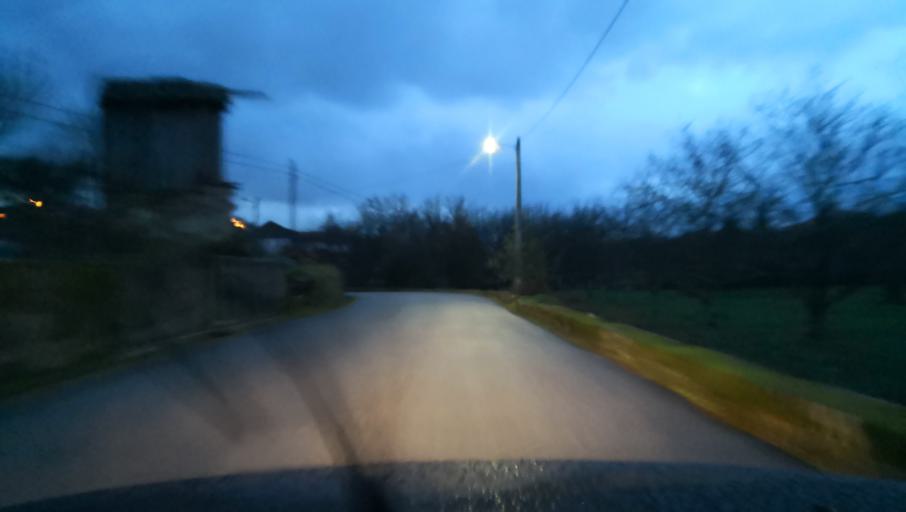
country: PT
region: Vila Real
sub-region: Vila Real
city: Vila Real
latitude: 41.3038
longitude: -7.7094
